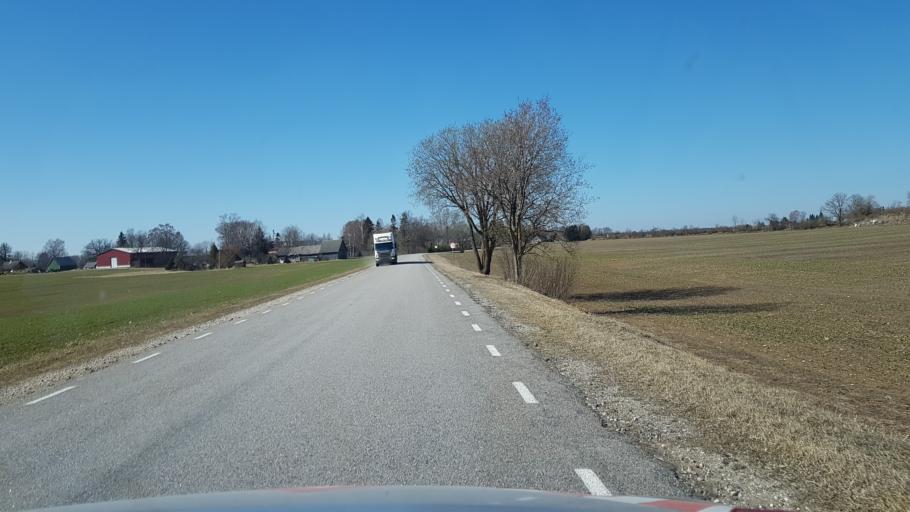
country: EE
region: Laeaene-Virumaa
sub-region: Vaeike-Maarja vald
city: Vaike-Maarja
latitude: 59.1067
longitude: 26.3834
